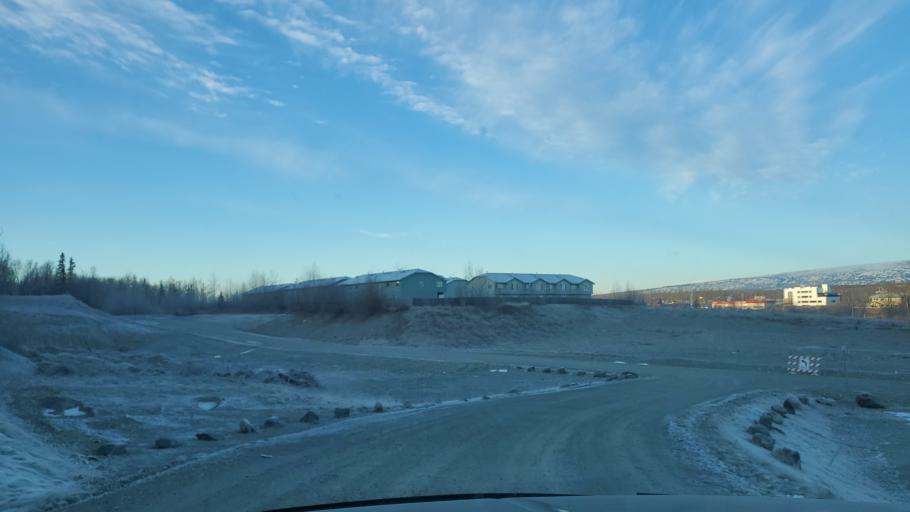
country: US
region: Alaska
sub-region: Matanuska-Susitna Borough
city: Wasilla
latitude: 61.5780
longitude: -149.4232
